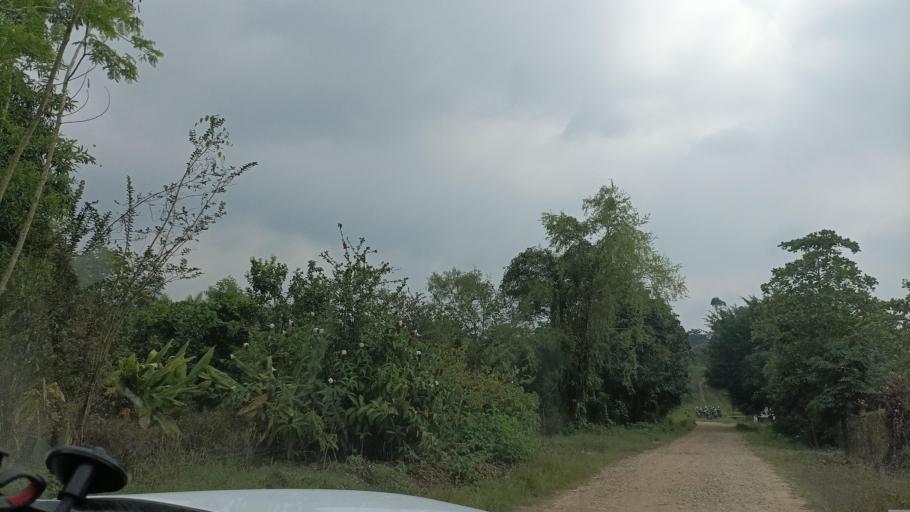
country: MX
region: Veracruz
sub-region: Moloacan
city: Cuichapa
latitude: 17.5792
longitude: -94.2301
